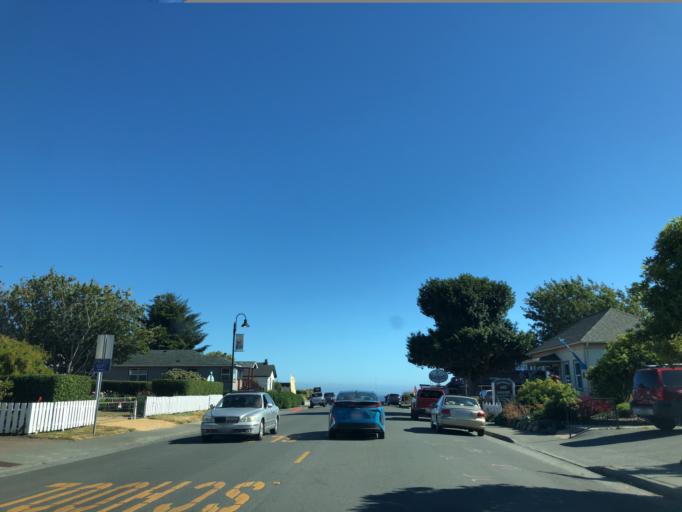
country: US
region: California
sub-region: Humboldt County
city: Westhaven-Moonstone
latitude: 41.0598
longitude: -124.1431
